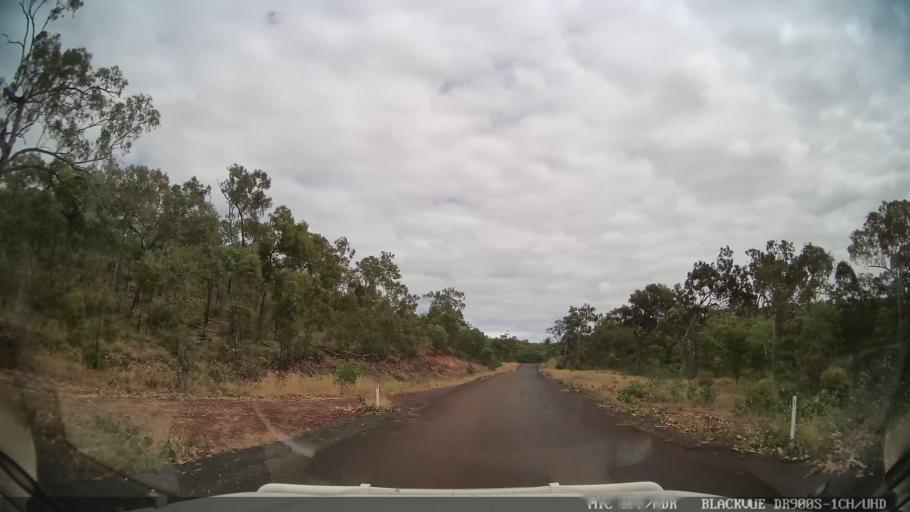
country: AU
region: Queensland
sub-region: Cook
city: Cooktown
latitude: -15.2817
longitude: 144.9116
